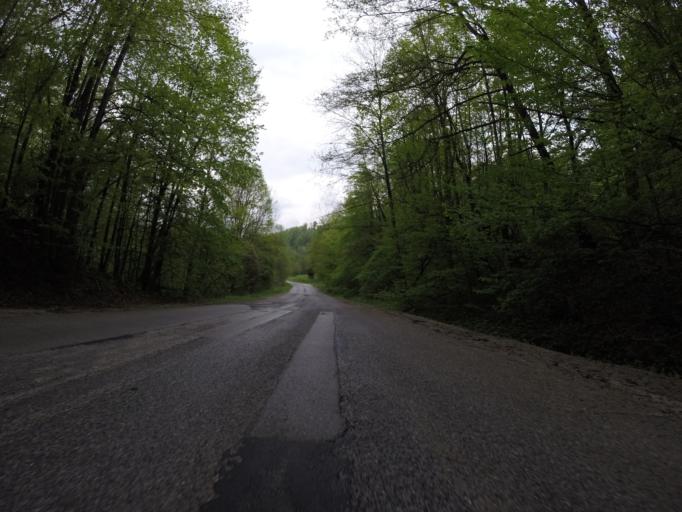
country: SK
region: Banskobystricky
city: Tisovec
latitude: 48.7090
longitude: 19.9946
